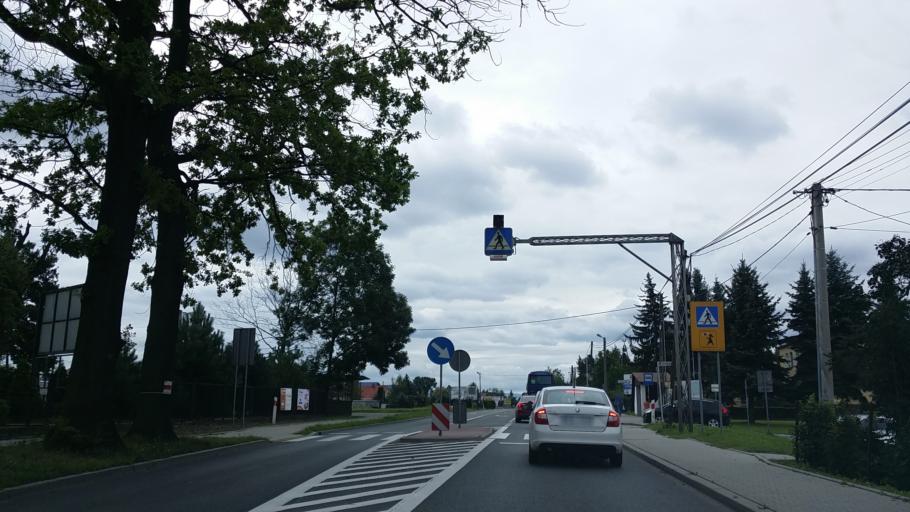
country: PL
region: Lesser Poland Voivodeship
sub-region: Powiat wadowicki
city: Tomice
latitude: 49.9009
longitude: 19.4849
